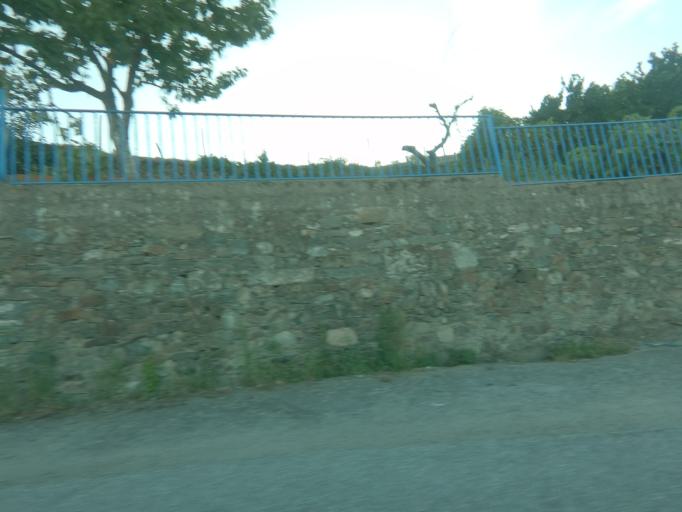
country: PT
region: Vila Real
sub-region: Peso da Regua
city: Godim
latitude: 41.1606
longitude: -7.8111
